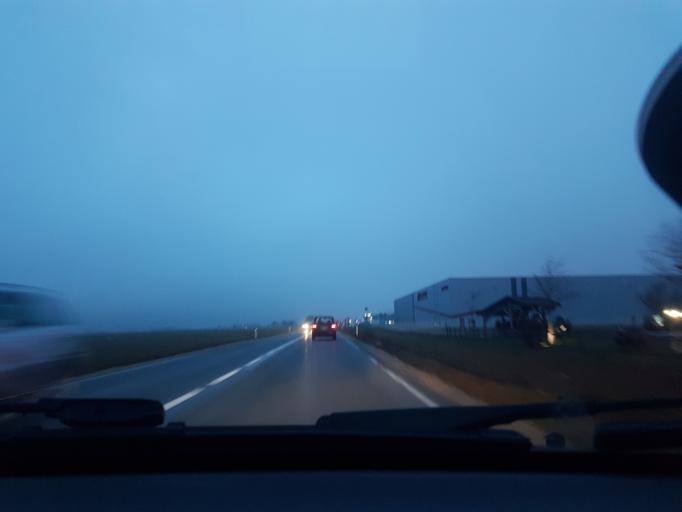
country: FR
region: Franche-Comte
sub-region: Departement du Doubs
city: Pontarlier
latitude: 46.9040
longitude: 6.3299
